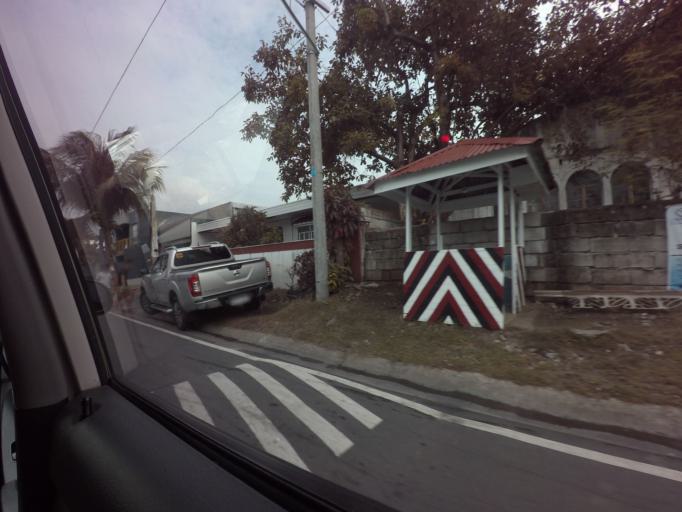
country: PH
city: Sambayanihan People's Village
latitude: 14.4479
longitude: 121.0233
